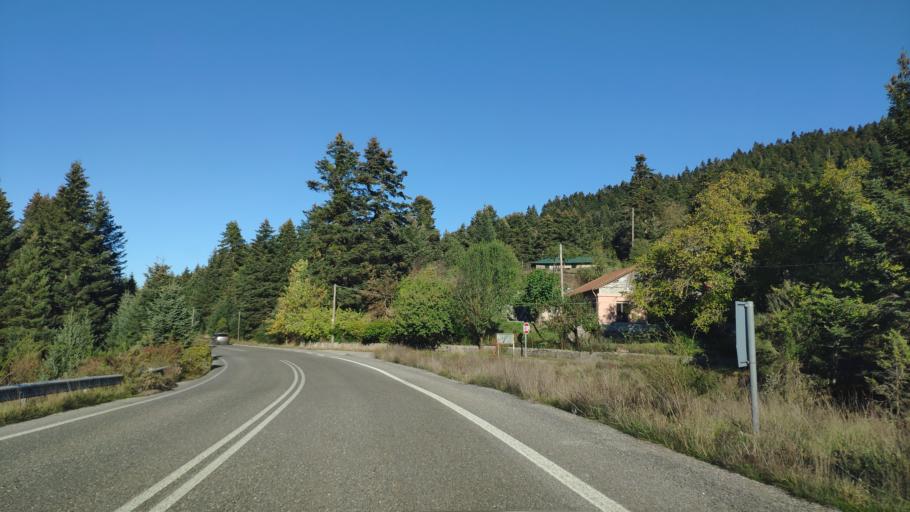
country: GR
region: Peloponnese
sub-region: Nomos Arkadias
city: Langadhia
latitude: 37.6519
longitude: 22.1231
